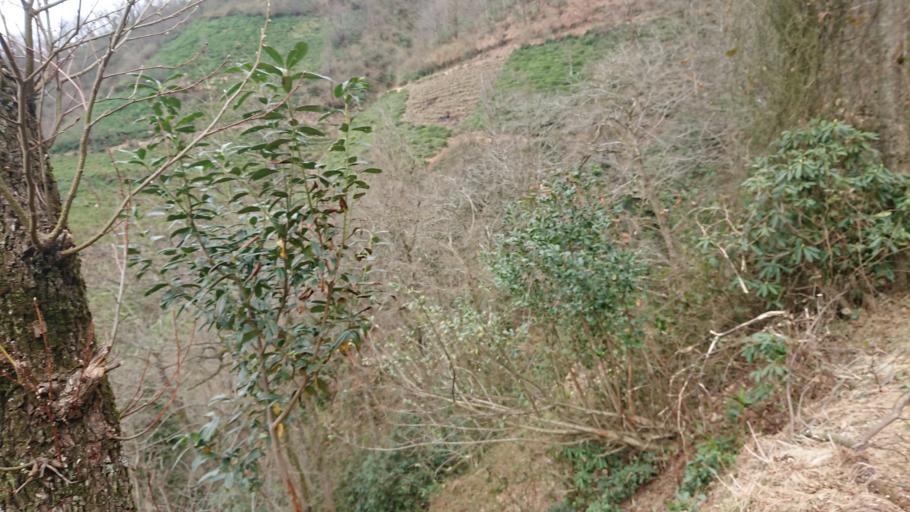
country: TR
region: Rize
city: Rize
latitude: 40.9844
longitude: 40.4978
